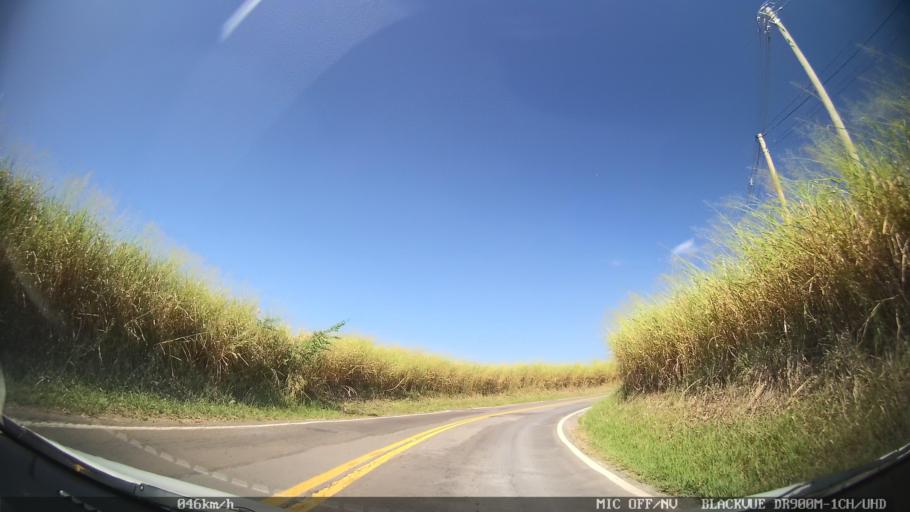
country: BR
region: Sao Paulo
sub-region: Valinhos
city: Valinhos
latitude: -23.0174
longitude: -47.0945
